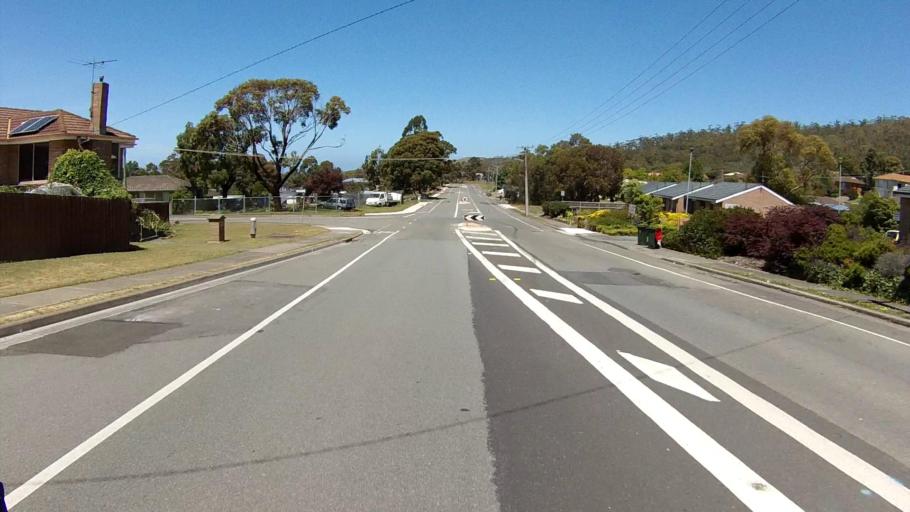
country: AU
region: Tasmania
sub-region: Clarence
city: Rokeby
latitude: -42.8936
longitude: 147.4313
